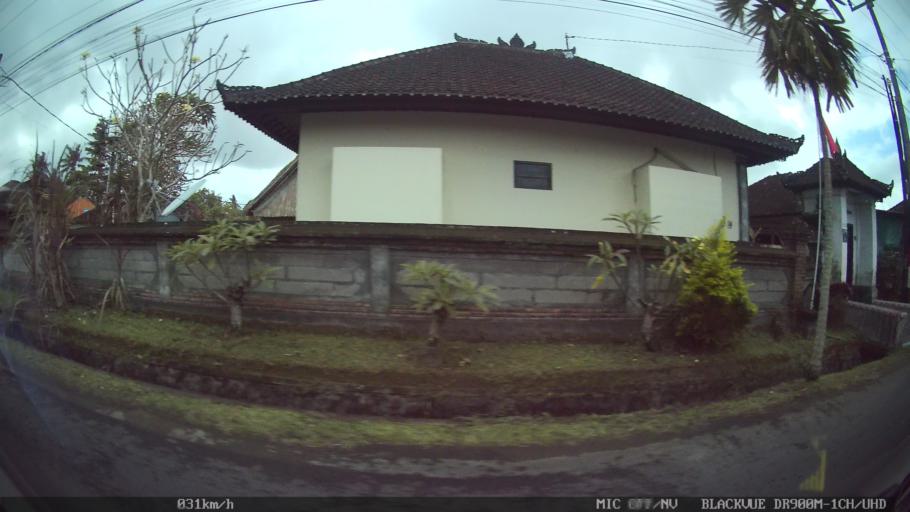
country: ID
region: Bali
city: Banjar Mambalkajanan
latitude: -8.5509
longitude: 115.2119
